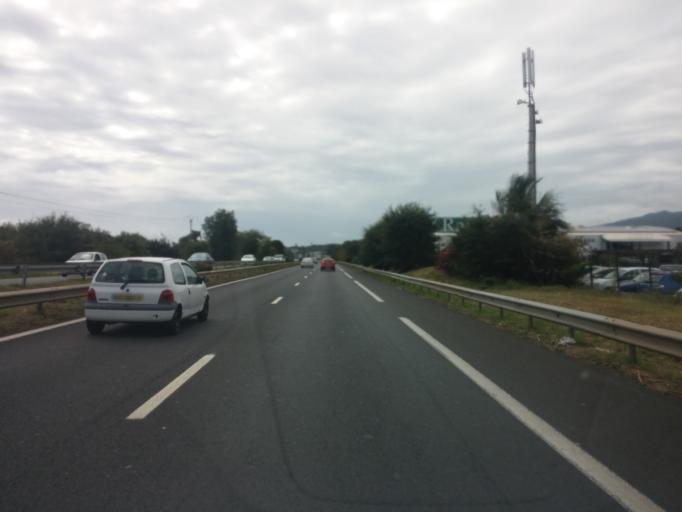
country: RE
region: Reunion
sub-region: Reunion
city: Saint-Paul
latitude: -20.9844
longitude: 55.2924
